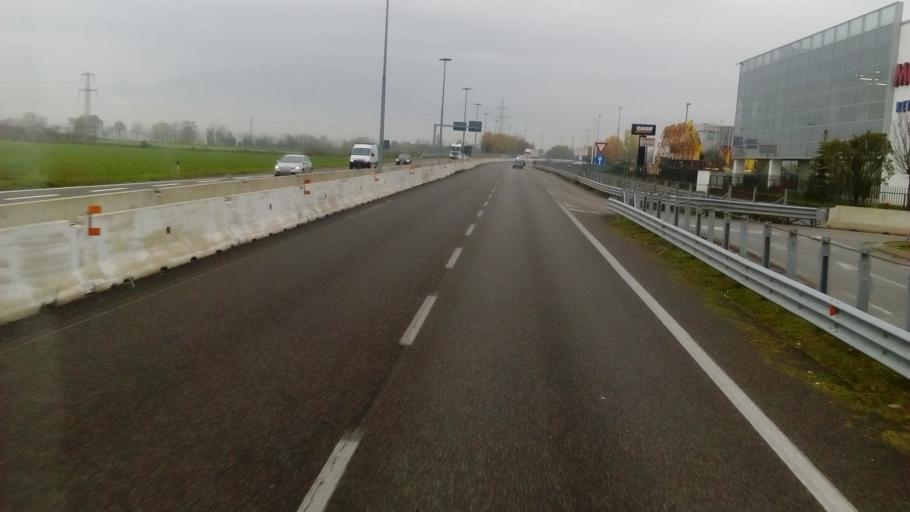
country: IT
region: Lombardy
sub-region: Provincia di Bergamo
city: Treviolo
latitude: 45.6716
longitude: 9.6010
